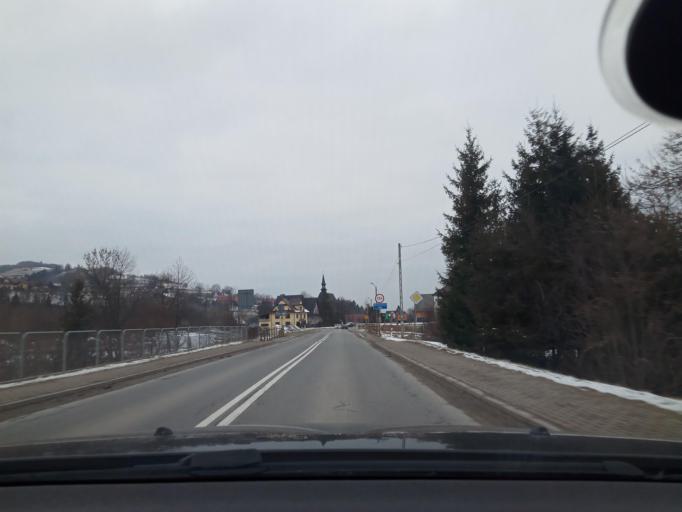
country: PL
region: Lesser Poland Voivodeship
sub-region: Powiat limanowski
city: Mszana Gorna
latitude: 49.6290
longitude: 20.1433
